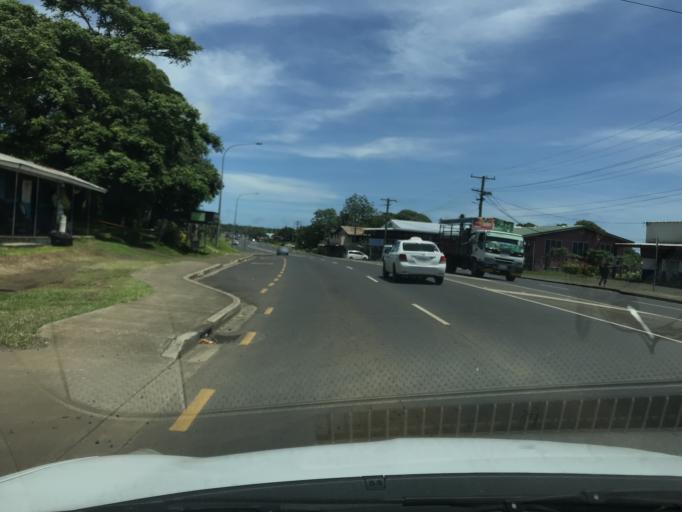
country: WS
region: Tuamasaga
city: Vaiusu
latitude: -13.8239
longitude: -171.7981
